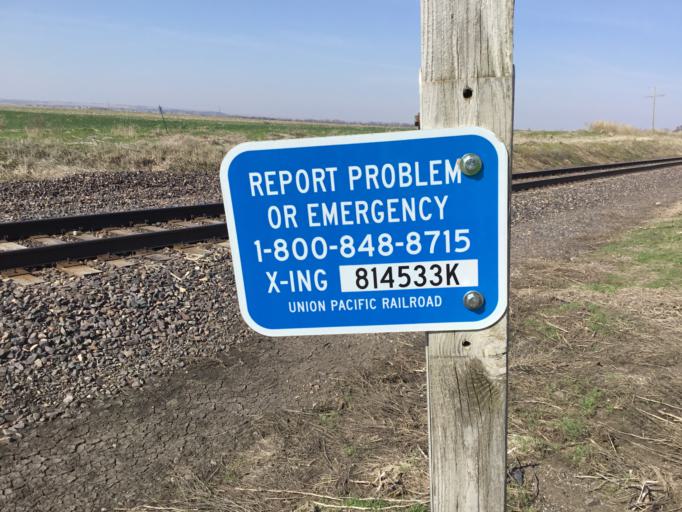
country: US
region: Kansas
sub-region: Ellsworth County
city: Ellsworth
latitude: 38.8105
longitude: -98.4120
